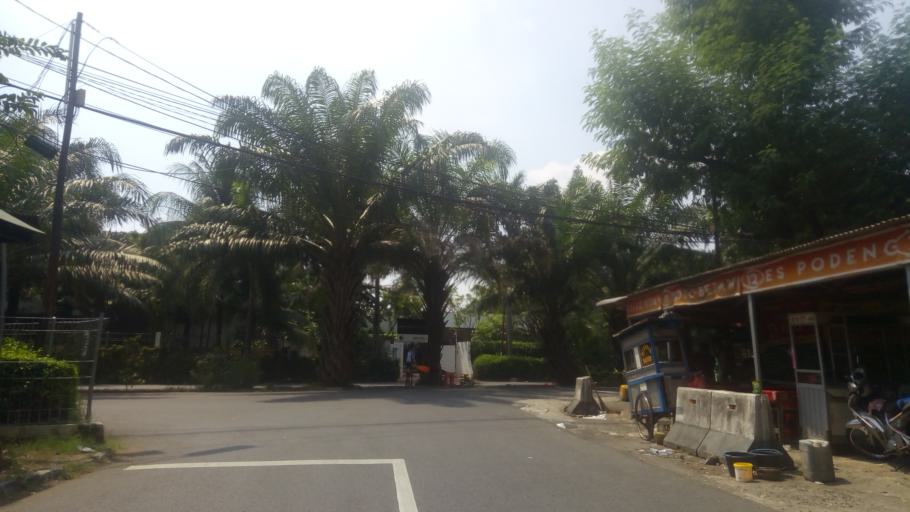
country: ID
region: Jakarta Raya
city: Jakarta
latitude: -6.2348
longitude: 106.8318
